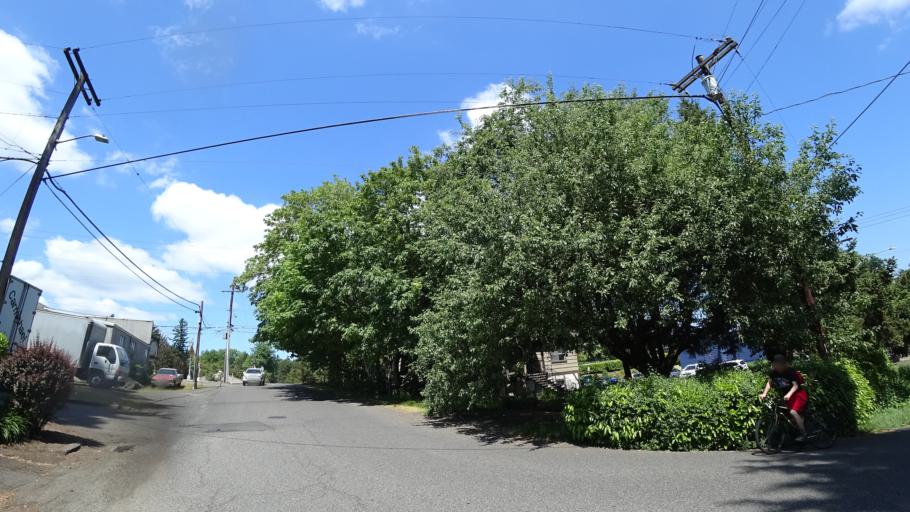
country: US
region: Oregon
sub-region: Clackamas County
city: Lake Oswego
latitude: 45.4651
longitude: -122.7026
